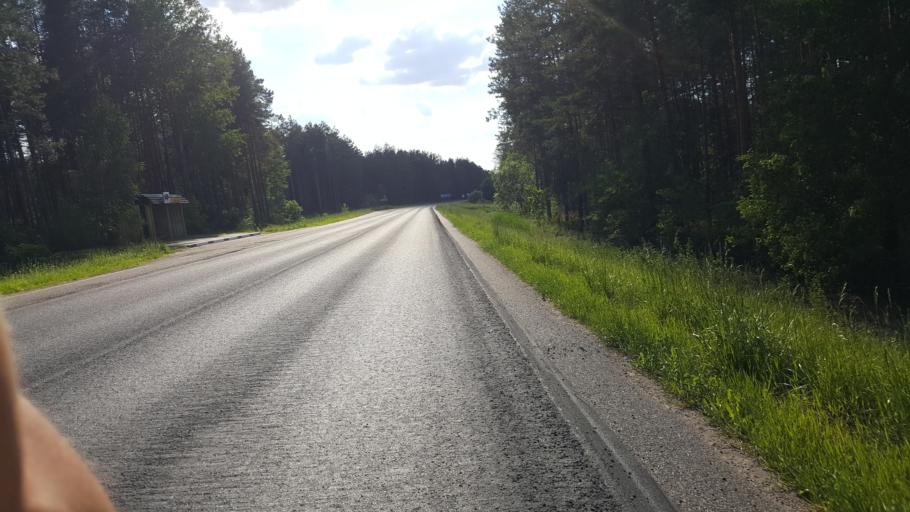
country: BY
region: Brest
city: Zhabinka
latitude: 52.3983
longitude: 24.0225
